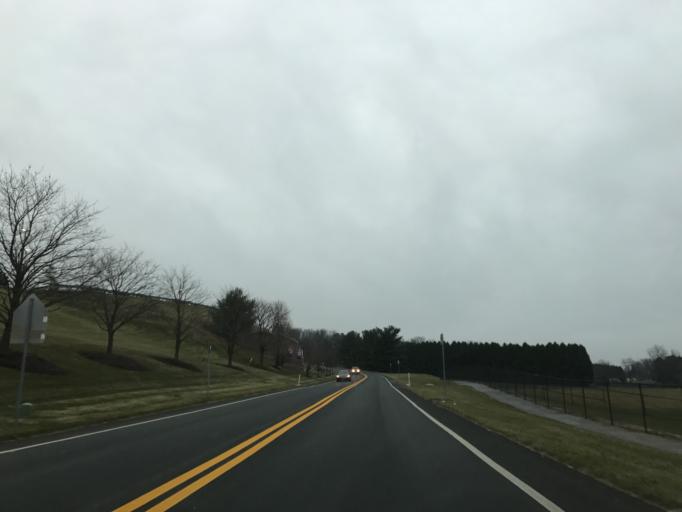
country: US
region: Maryland
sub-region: Carroll County
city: Westminster
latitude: 39.5586
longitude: -76.9924
